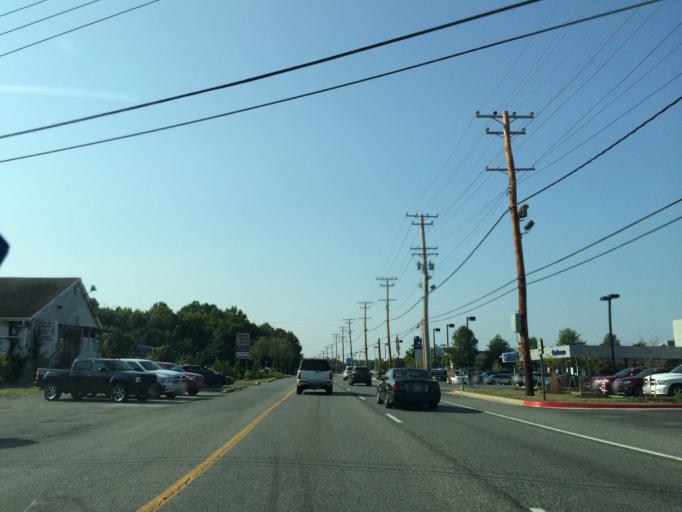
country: US
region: Maryland
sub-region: Prince George's County
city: Bowie
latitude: 38.9236
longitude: -76.7174
